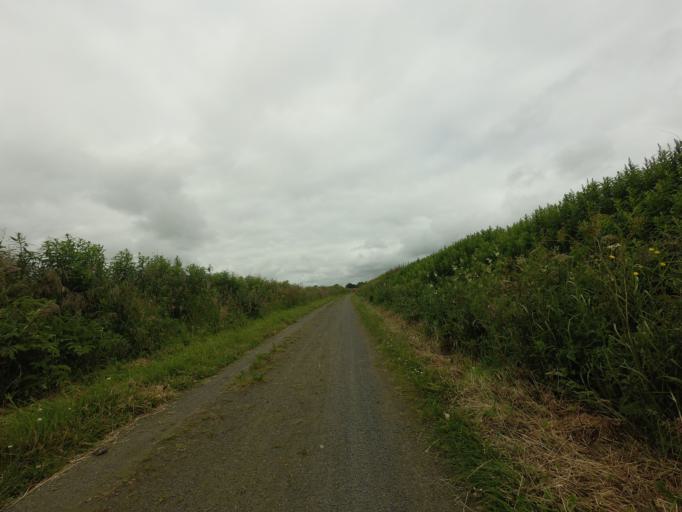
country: GB
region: Scotland
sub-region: Aberdeenshire
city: Ellon
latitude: 57.4837
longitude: -2.1349
